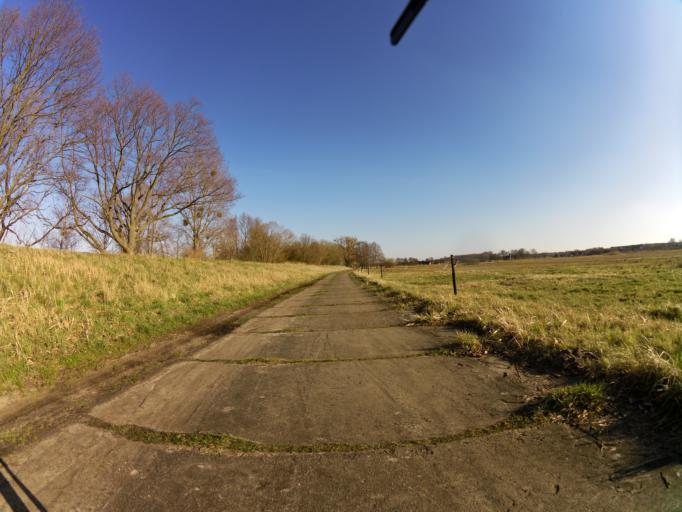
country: PL
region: West Pomeranian Voivodeship
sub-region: Powiat policki
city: Nowe Warpno
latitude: 53.7036
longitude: 14.3602
